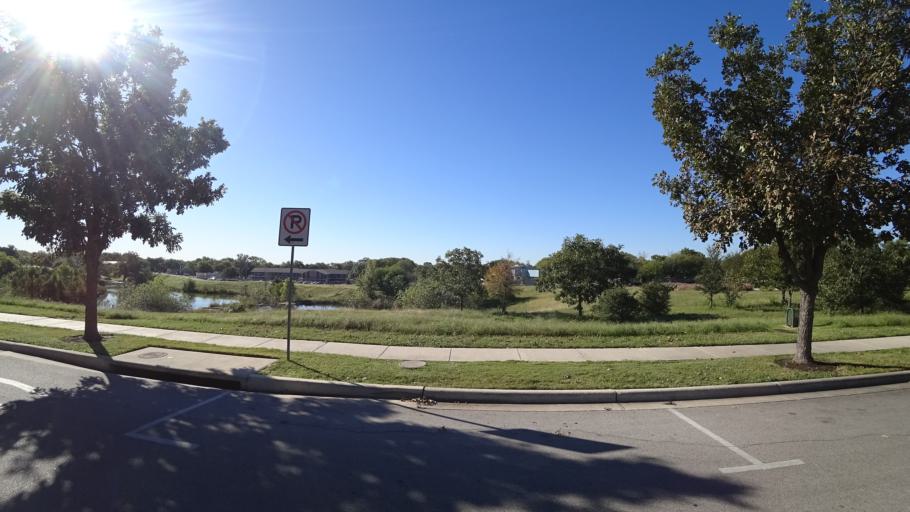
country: US
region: Texas
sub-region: Travis County
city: Austin
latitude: 30.2898
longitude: -97.7035
